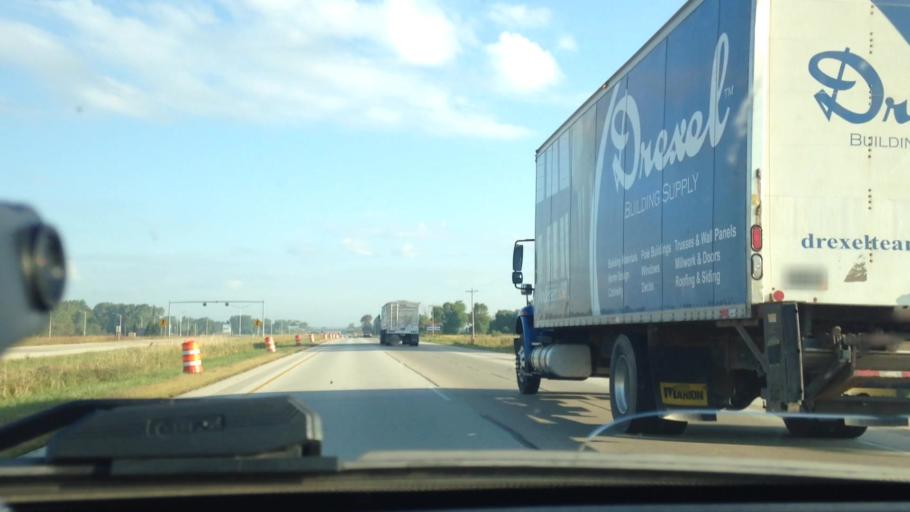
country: US
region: Wisconsin
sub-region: Brown County
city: Suamico
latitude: 44.7382
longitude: -88.0506
